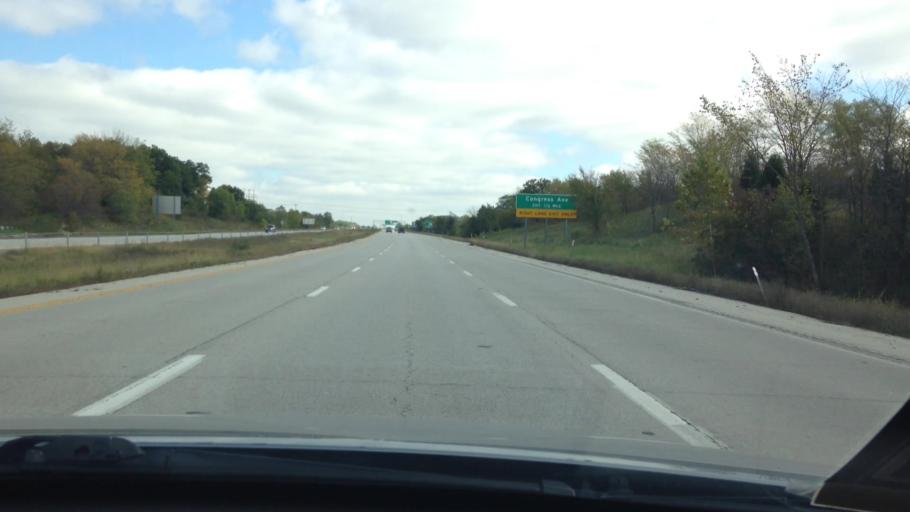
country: US
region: Missouri
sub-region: Platte County
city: Weatherby Lake
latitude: 39.2538
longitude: -94.6818
